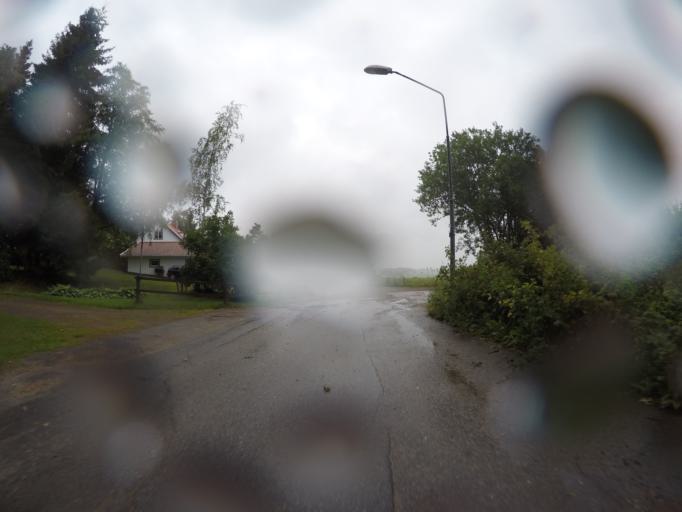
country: SE
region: Vaestra Goetaland
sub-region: Trollhattan
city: Sjuntorp
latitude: 58.1625
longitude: 12.3049
